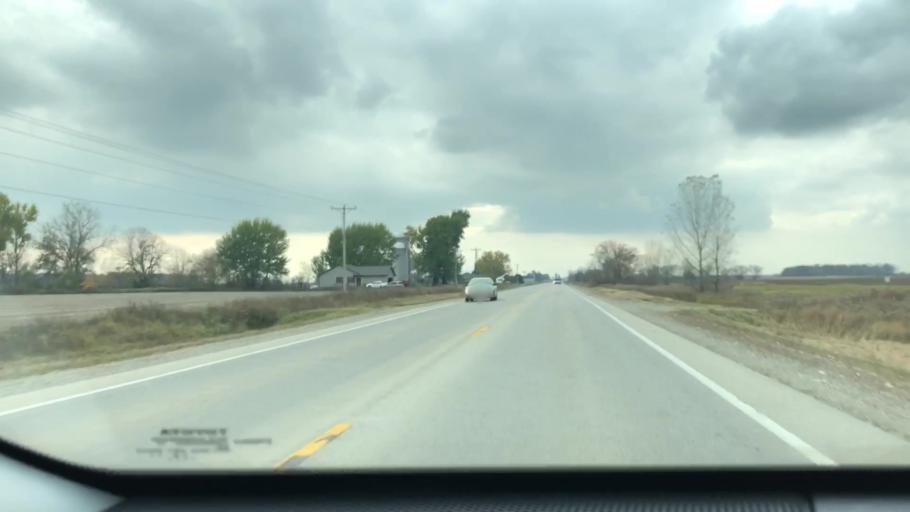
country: US
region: Wisconsin
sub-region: Outagamie County
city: Seymour
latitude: 44.5009
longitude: -88.2786
